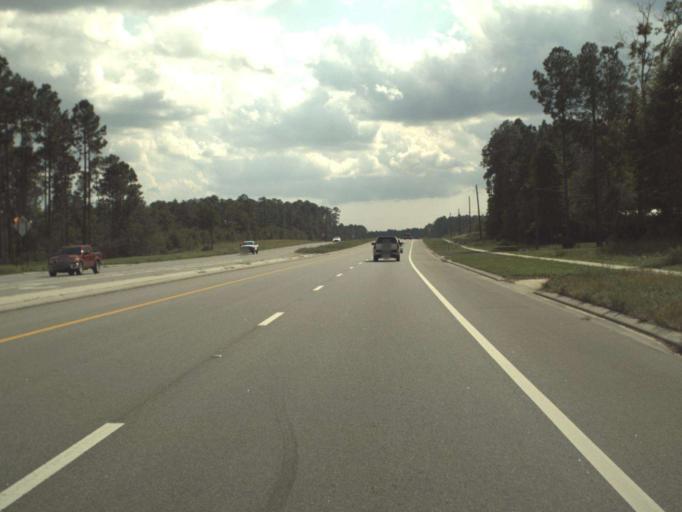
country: US
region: Florida
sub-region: Bay County
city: Laguna Beach
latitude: 30.4351
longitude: -85.8742
